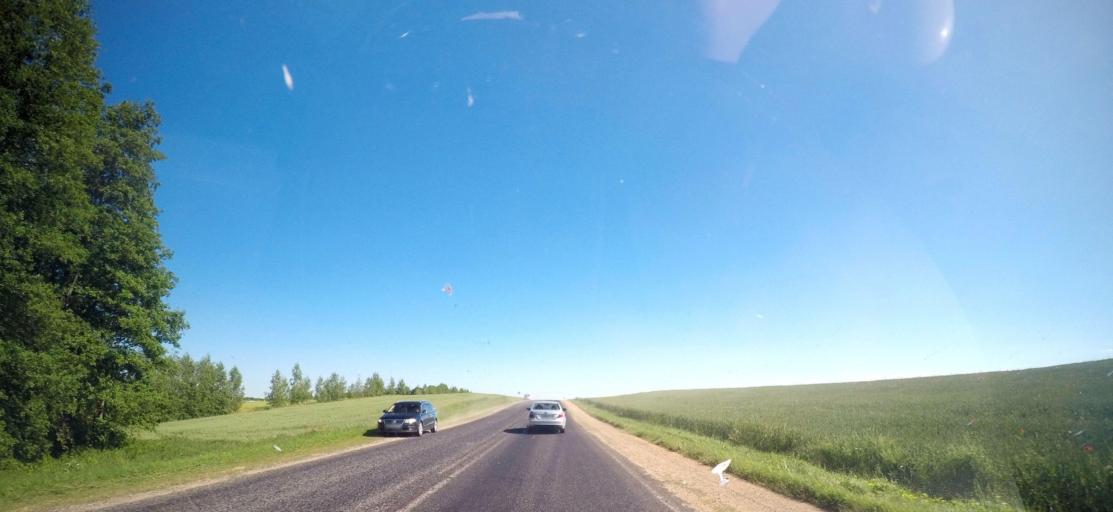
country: BY
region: Grodnenskaya
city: Vyalikaya Byerastavitsa
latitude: 53.2166
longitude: 23.9995
